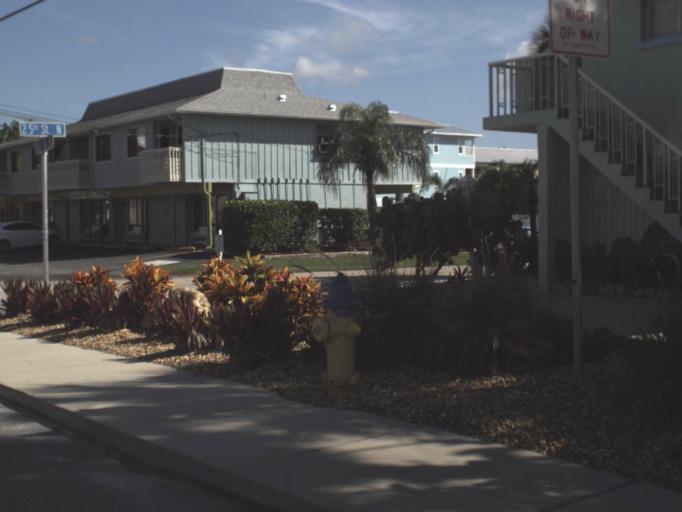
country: US
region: Florida
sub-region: Manatee County
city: Bradenton Beach
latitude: 27.4817
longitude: -82.7047
